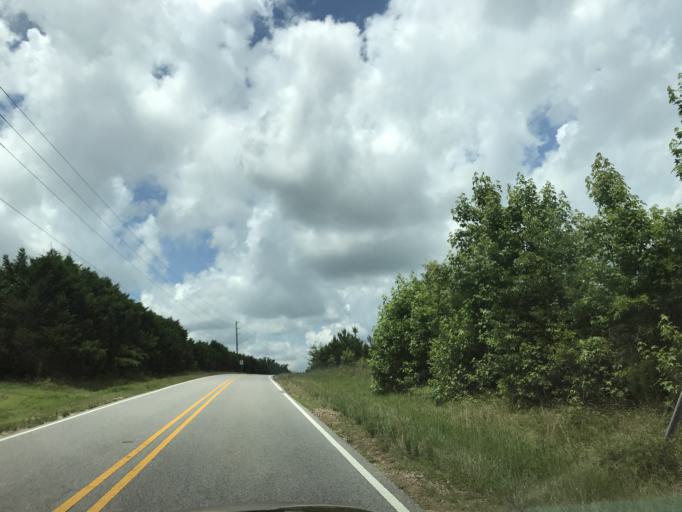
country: US
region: North Carolina
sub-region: Wake County
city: Rolesville
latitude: 35.9577
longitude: -78.3975
